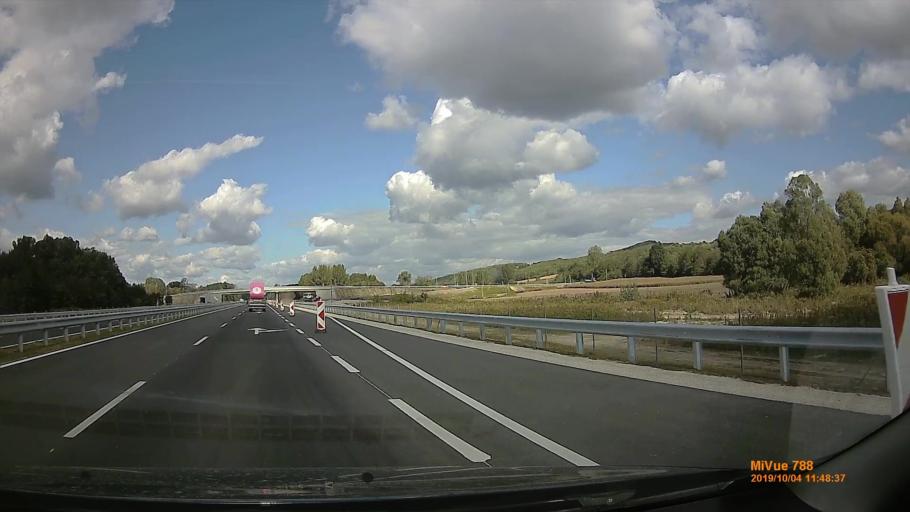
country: HU
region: Somogy
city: Karad
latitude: 46.6642
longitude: 17.7838
